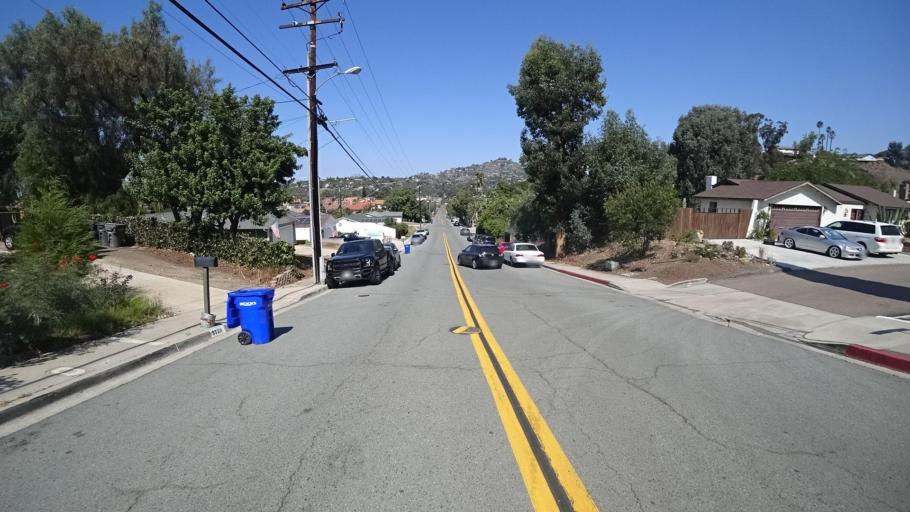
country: US
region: California
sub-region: San Diego County
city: Spring Valley
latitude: 32.7413
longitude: -116.9885
